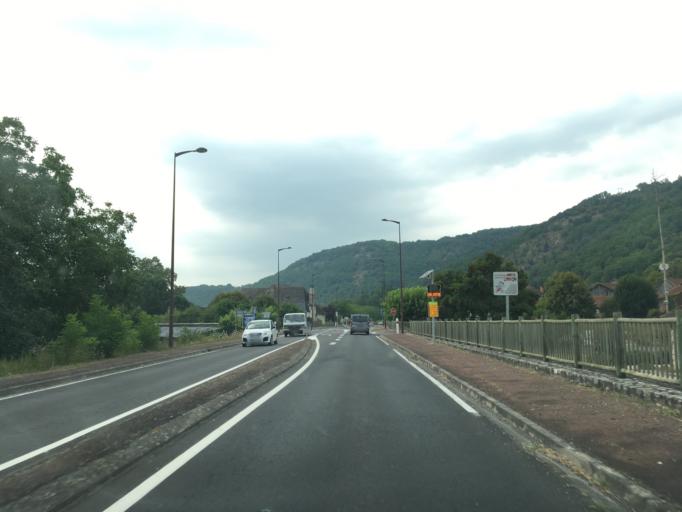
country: FR
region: Midi-Pyrenees
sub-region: Departement du Lot
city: Souillac
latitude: 44.8852
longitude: 1.4096
